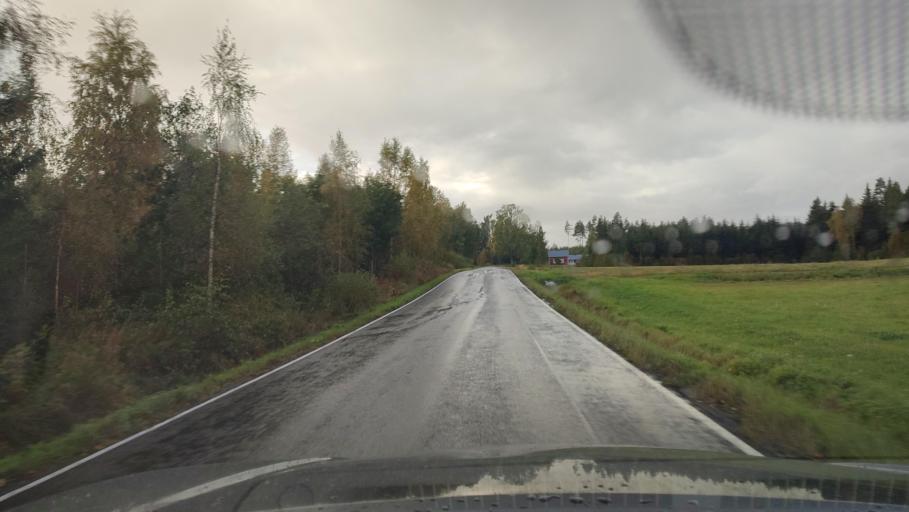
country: FI
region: Southern Ostrobothnia
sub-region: Suupohja
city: Karijoki
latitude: 62.3162
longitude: 21.6885
